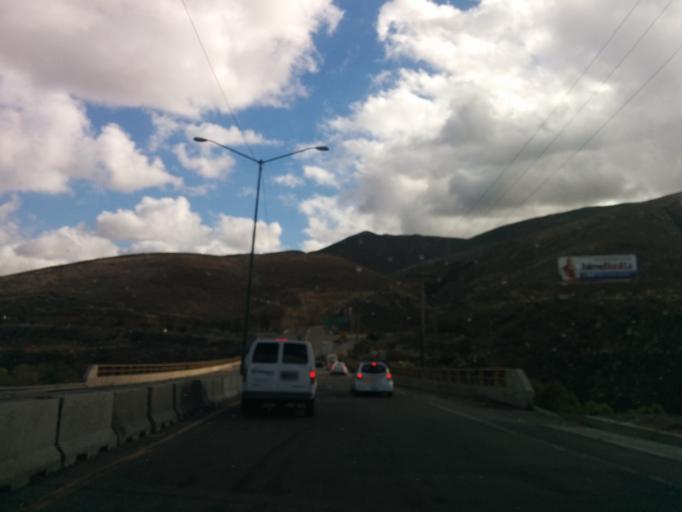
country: MX
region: Baja California
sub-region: Tijuana
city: Ejido Javier Rojo Gomez
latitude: 32.5423
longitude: -116.8587
